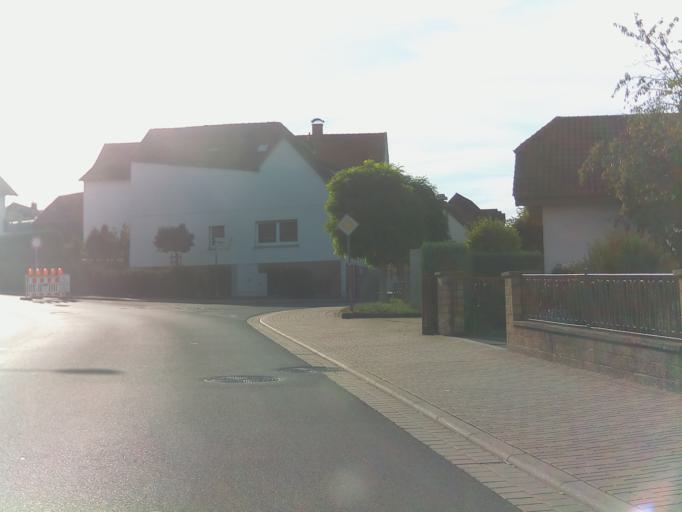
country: DE
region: Hesse
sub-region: Regierungsbezirk Kassel
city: Neuhof
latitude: 50.4548
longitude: 9.6119
